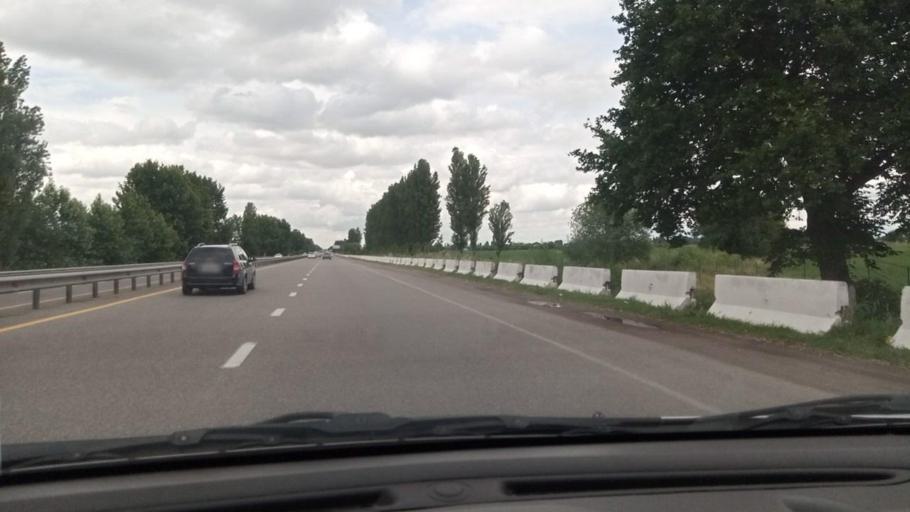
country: UZ
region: Toshkent Shahri
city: Bektemir
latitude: 41.2100
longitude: 69.4028
